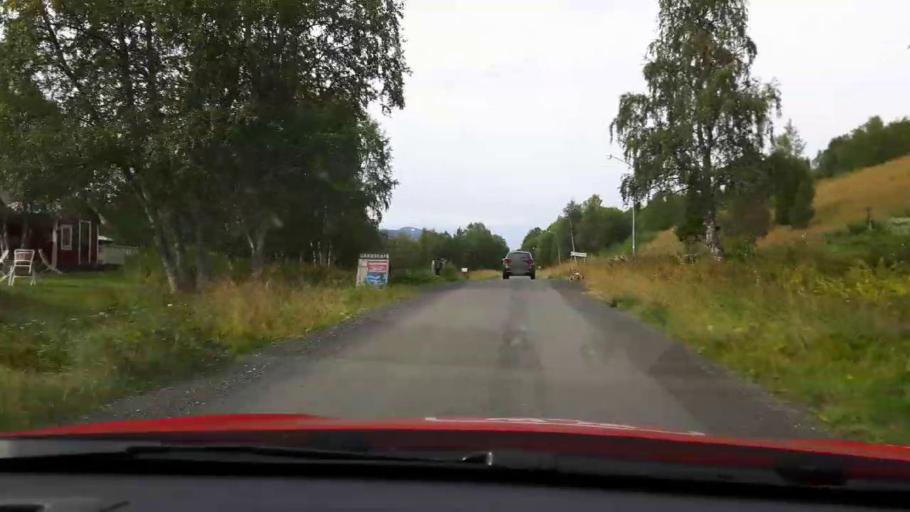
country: SE
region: Jaemtland
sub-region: Are Kommun
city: Are
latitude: 63.7481
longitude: 12.9657
